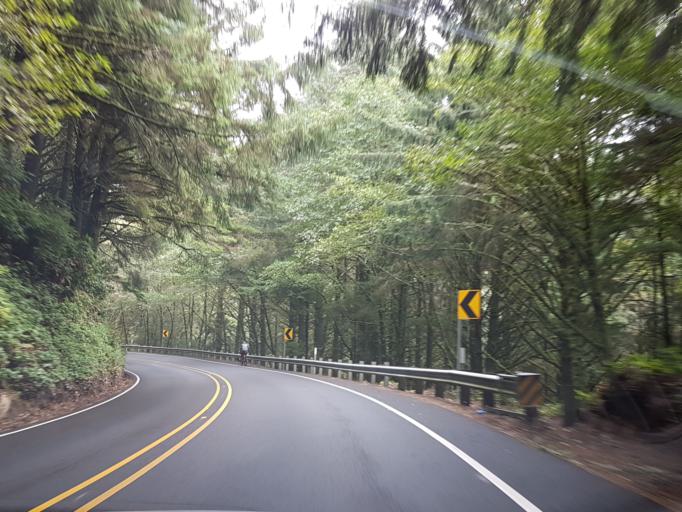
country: US
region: Oregon
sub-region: Lane County
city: Florence
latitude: 44.1189
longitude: -124.1210
